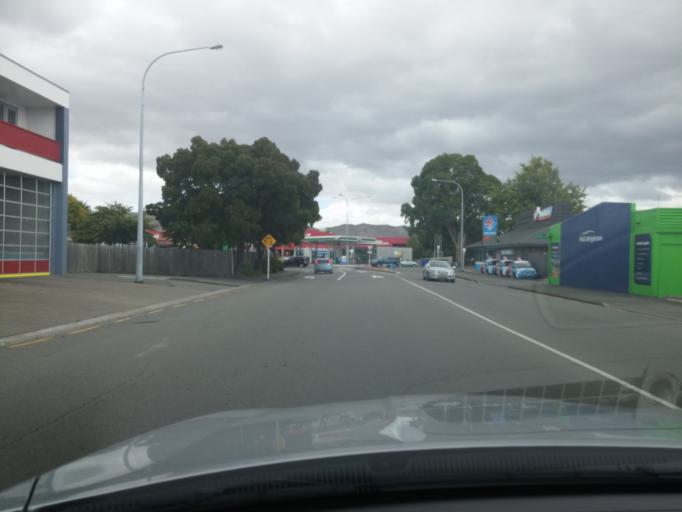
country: NZ
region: Marlborough
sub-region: Marlborough District
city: Blenheim
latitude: -41.5128
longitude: 173.9587
